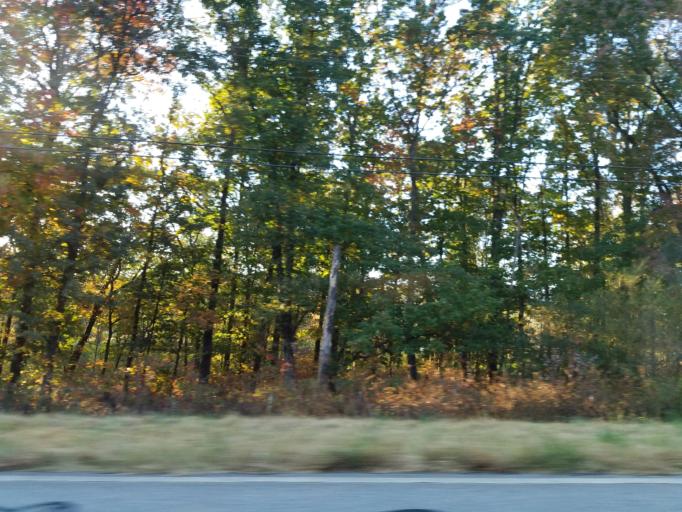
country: US
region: Georgia
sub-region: Dawson County
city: Dawsonville
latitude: 34.5381
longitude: -84.1678
